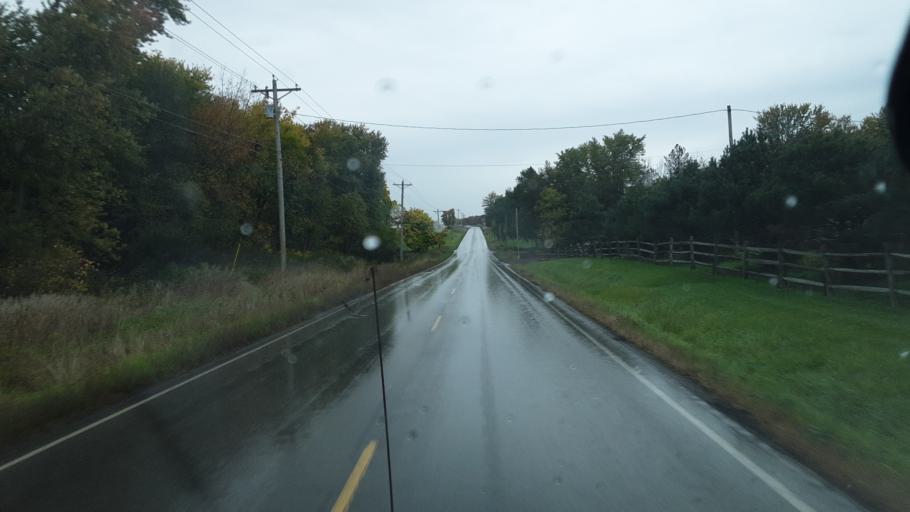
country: US
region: Ohio
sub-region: Wayne County
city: West Salem
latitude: 40.9385
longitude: -82.0819
